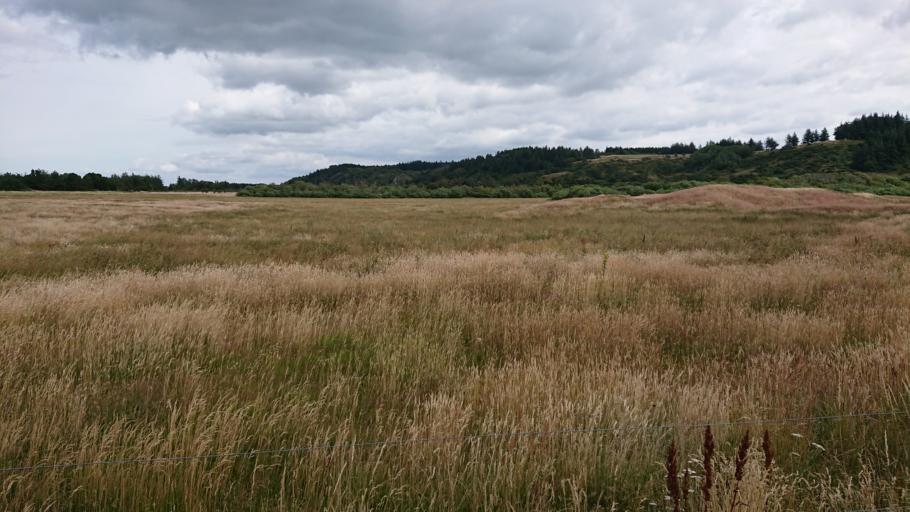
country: DK
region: North Denmark
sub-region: Jammerbugt Kommune
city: Brovst
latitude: 57.1382
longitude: 9.4101
